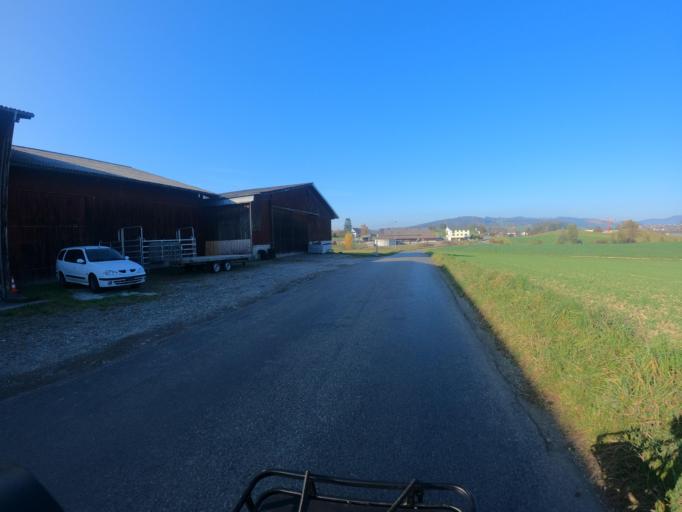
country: CH
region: Zurich
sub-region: Bezirk Affoltern
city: Obfelden / Toussen
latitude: 47.2826
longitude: 8.4315
